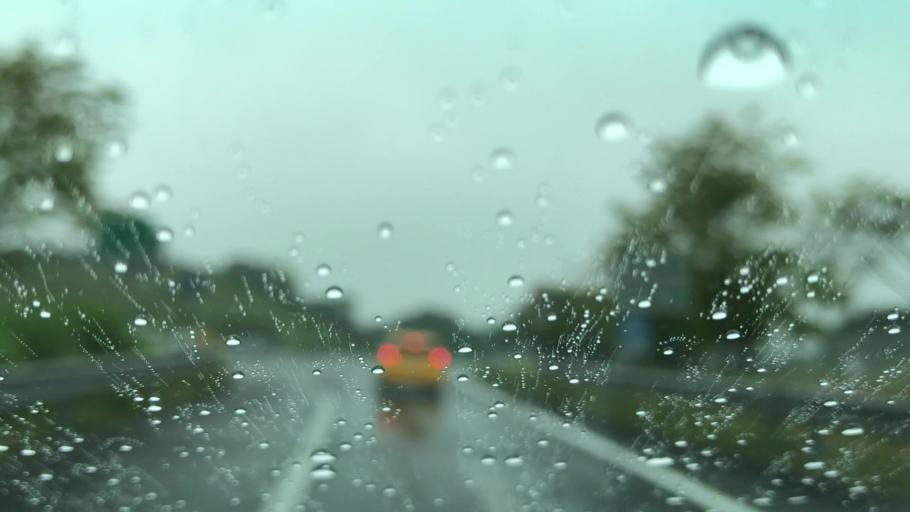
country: JP
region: Hokkaido
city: Shiraoi
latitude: 42.6106
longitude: 141.4648
